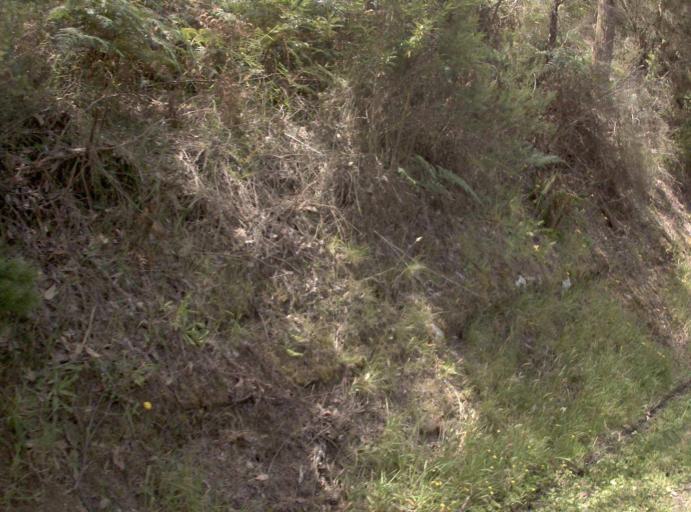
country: AU
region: Victoria
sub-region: Bass Coast
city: North Wonthaggi
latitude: -38.7305
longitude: 146.1222
